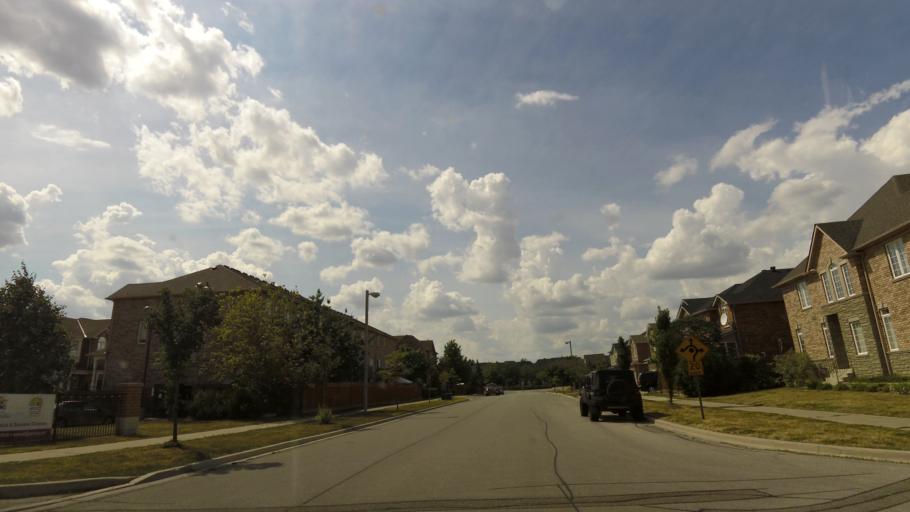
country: CA
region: Ontario
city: Vaughan
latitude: 43.7928
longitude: -79.5537
